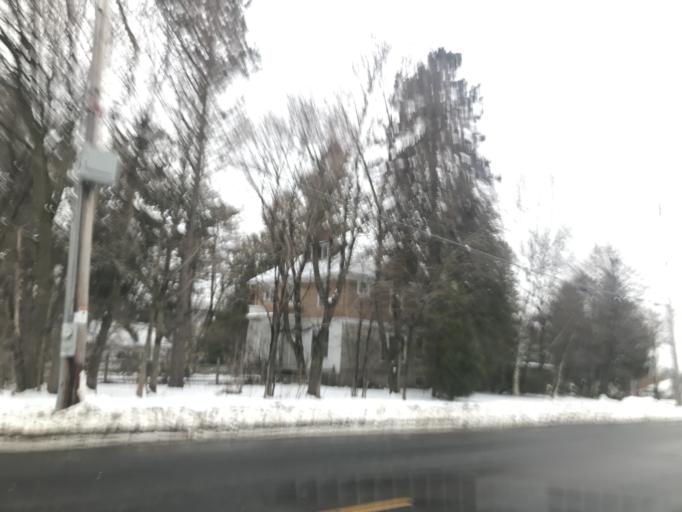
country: US
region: Wisconsin
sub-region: Door County
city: Sturgeon Bay
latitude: 44.8352
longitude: -87.3711
